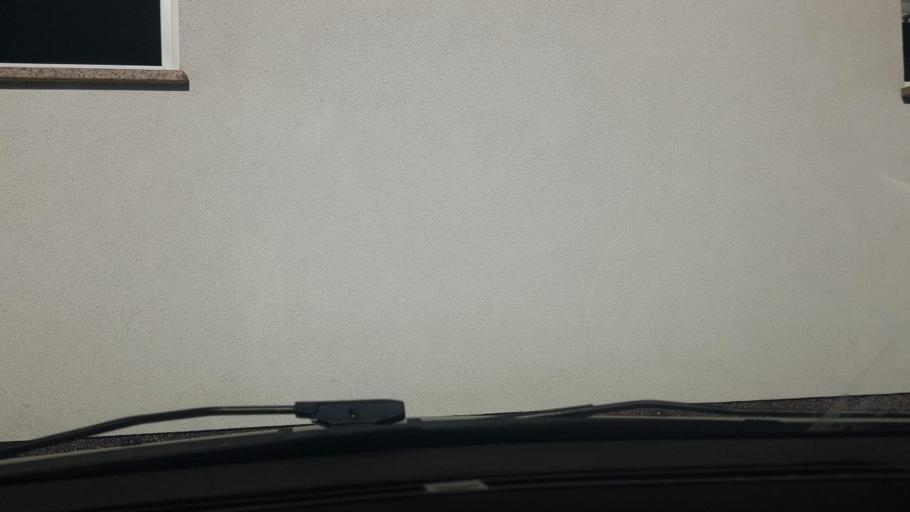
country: HR
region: Grad Zagreb
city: Novi Zagreb
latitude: 45.7597
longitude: 15.9642
